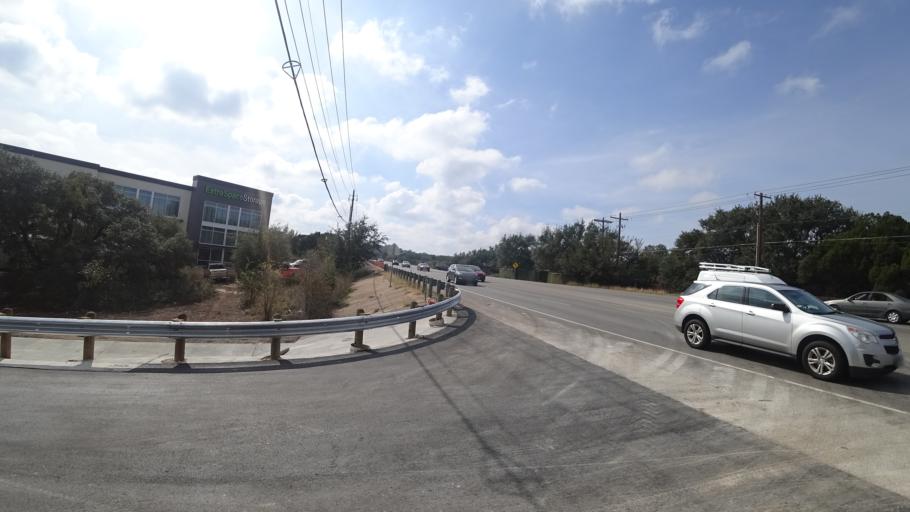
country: US
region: Texas
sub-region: Travis County
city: Hudson Bend
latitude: 30.3891
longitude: -97.9409
